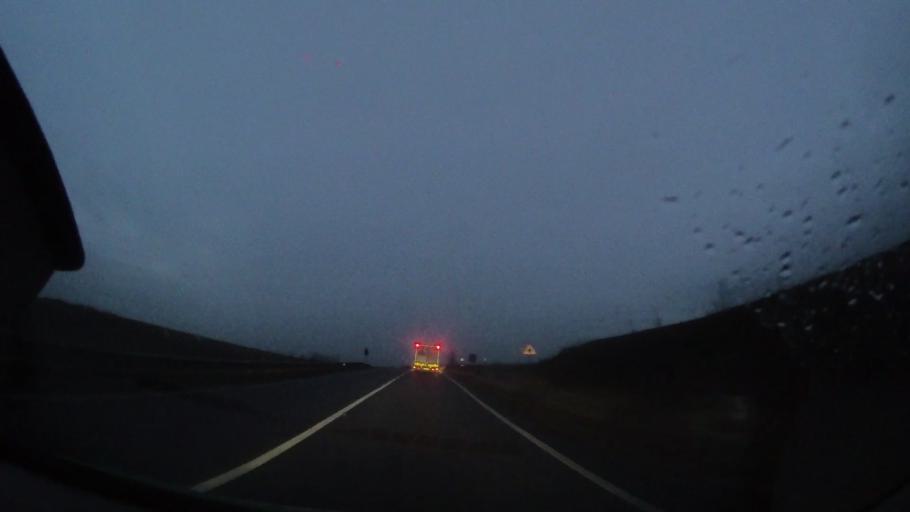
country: RO
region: Harghita
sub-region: Comuna Subcetate
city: Subcetate
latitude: 46.8404
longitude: 25.4787
